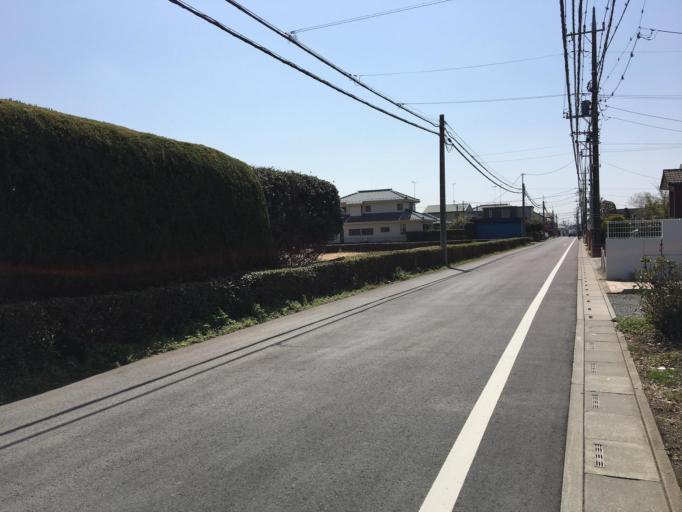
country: JP
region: Saitama
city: Sakado
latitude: 35.9085
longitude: 139.3656
